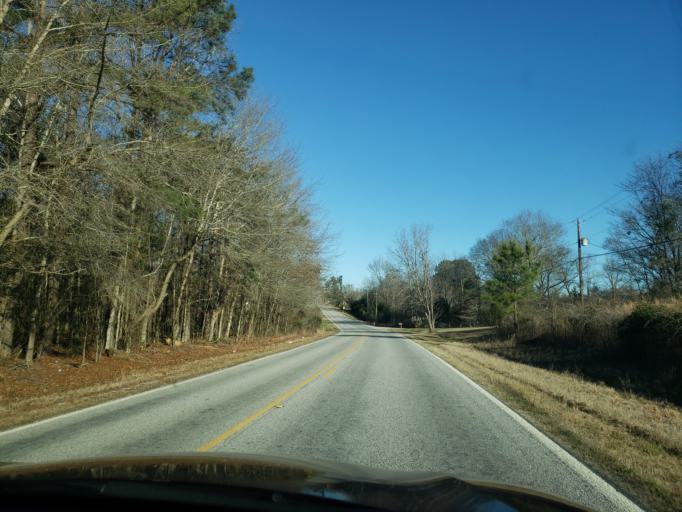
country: US
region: Alabama
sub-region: Elmore County
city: Tallassee
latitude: 32.5979
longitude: -85.8011
